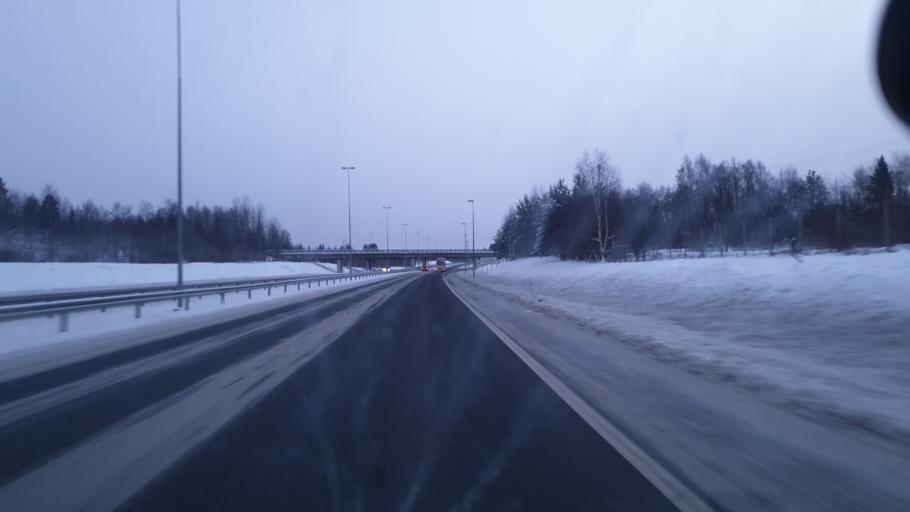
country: FI
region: Lapland
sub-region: Kemi-Tornio
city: Tornio
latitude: 65.8368
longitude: 24.2731
